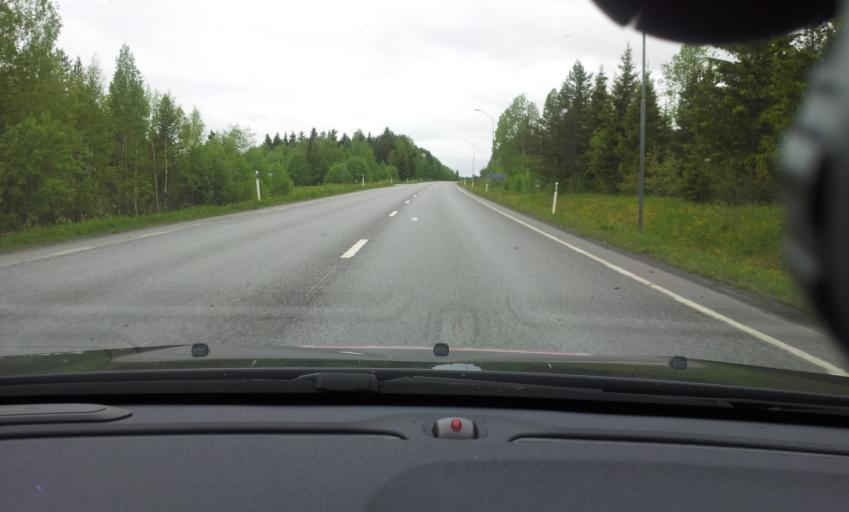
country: SE
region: Jaemtland
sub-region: Krokoms Kommun
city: Valla
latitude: 63.3243
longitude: 14.0520
